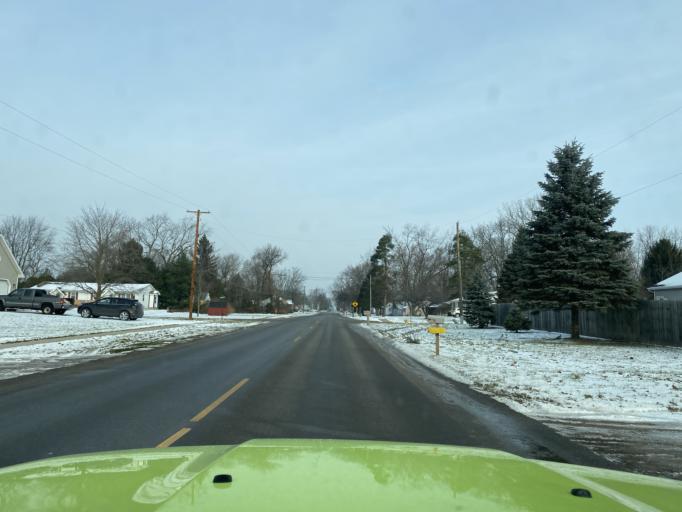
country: US
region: Michigan
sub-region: Ottawa County
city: Allendale
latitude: 42.9692
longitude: -85.9242
